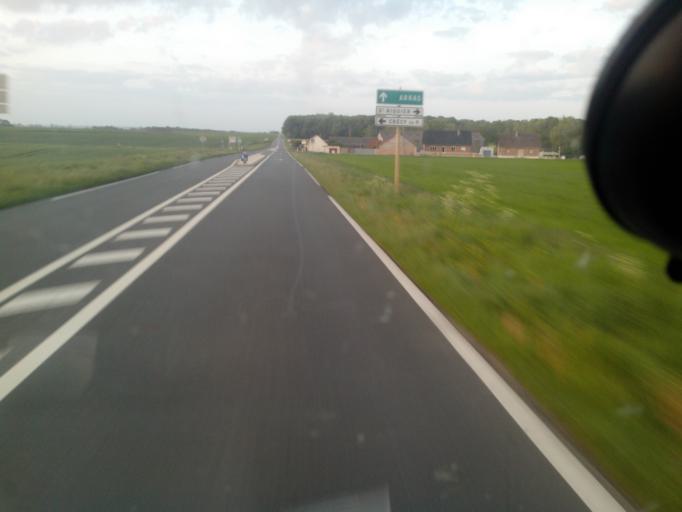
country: FR
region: Picardie
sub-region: Departement de la Somme
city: Crecy-en-Ponthieu
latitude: 50.2121
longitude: 1.9094
